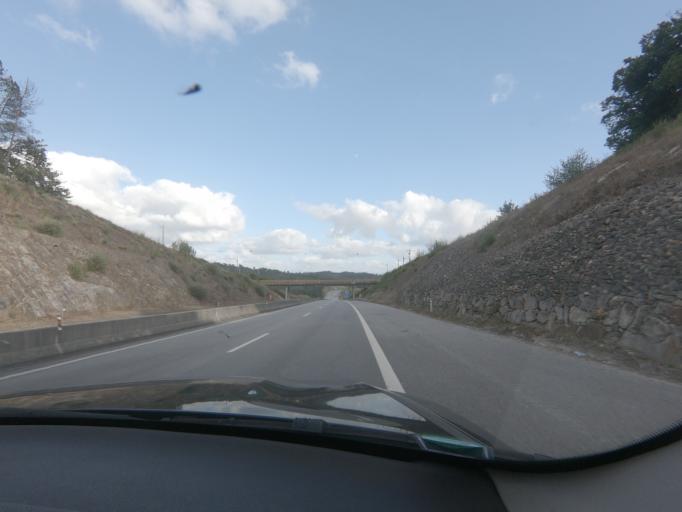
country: PT
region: Viseu
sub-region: Viseu
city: Abraveses
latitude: 40.6454
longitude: -7.9653
